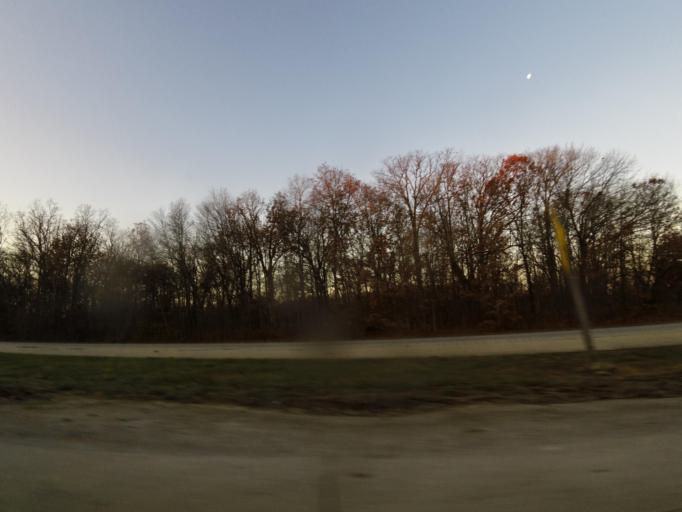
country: US
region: Illinois
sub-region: Marion County
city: Salem
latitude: 38.5982
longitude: -88.9655
